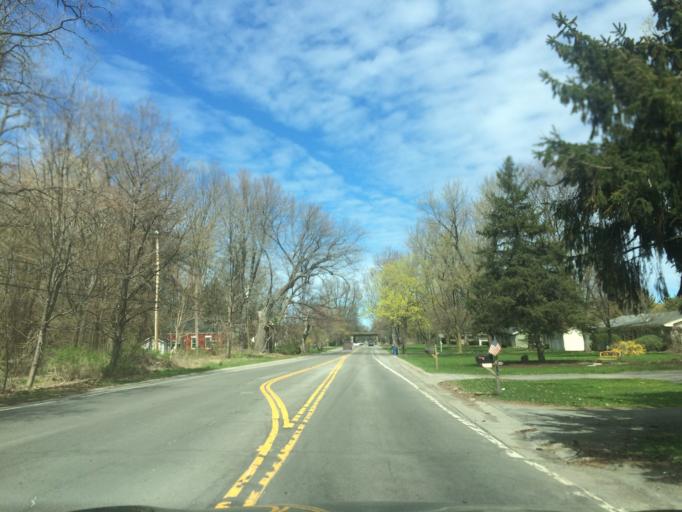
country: US
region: New York
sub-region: Monroe County
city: Pittsford
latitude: 43.0816
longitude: -77.4937
